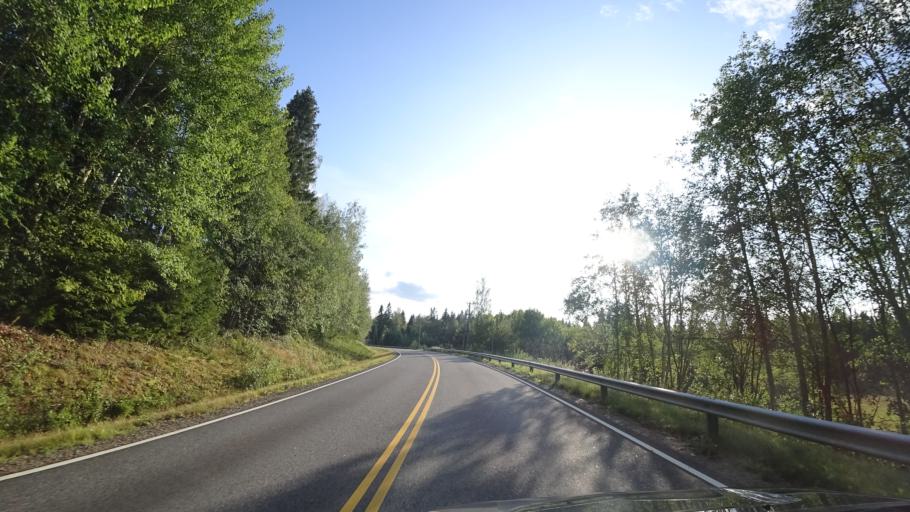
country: FI
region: Paijanne Tavastia
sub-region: Lahti
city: Hollola
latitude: 61.1313
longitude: 25.2941
